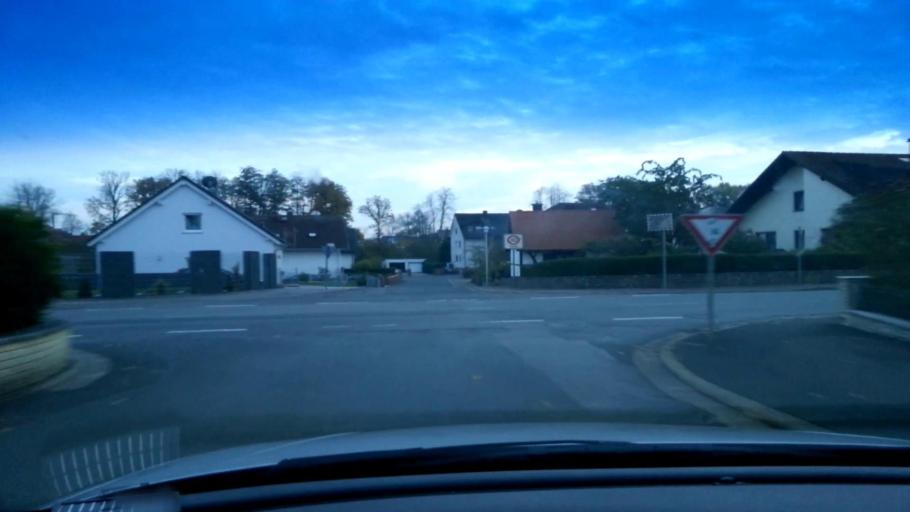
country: DE
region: Bavaria
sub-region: Upper Franconia
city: Breitengussbach
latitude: 49.9710
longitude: 10.8919
